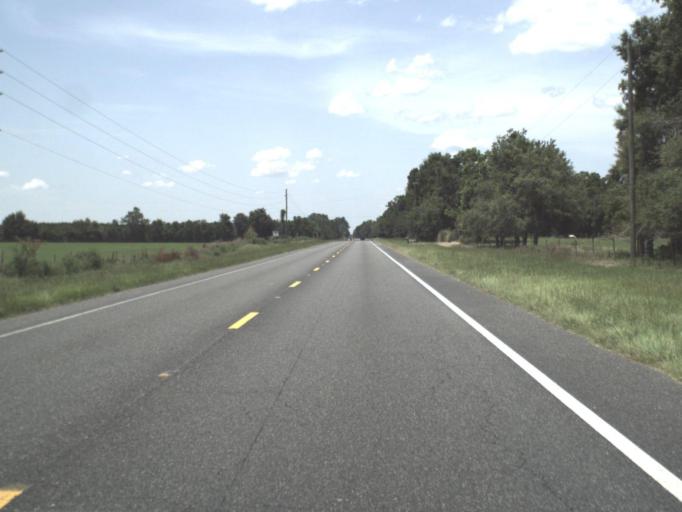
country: US
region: Florida
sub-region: Gilchrist County
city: Trenton
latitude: 29.5406
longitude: -82.8228
